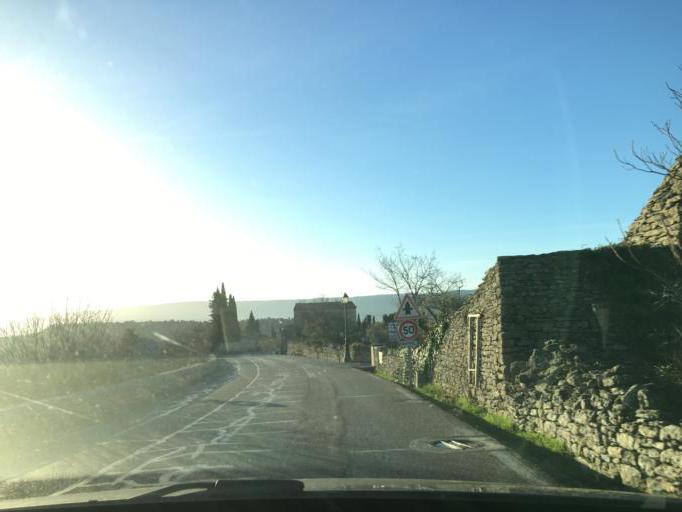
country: FR
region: Provence-Alpes-Cote d'Azur
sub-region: Departement du Vaucluse
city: Gordes
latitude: 43.9096
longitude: 5.1973
